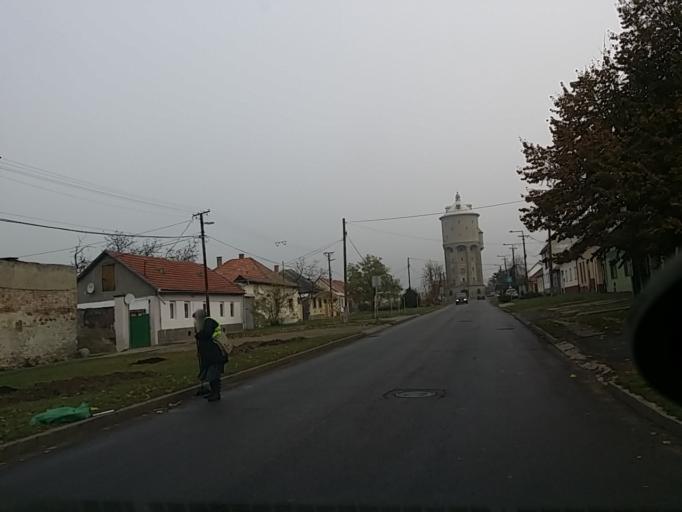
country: HU
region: Heves
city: Gyongyos
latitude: 47.7922
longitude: 19.9284
